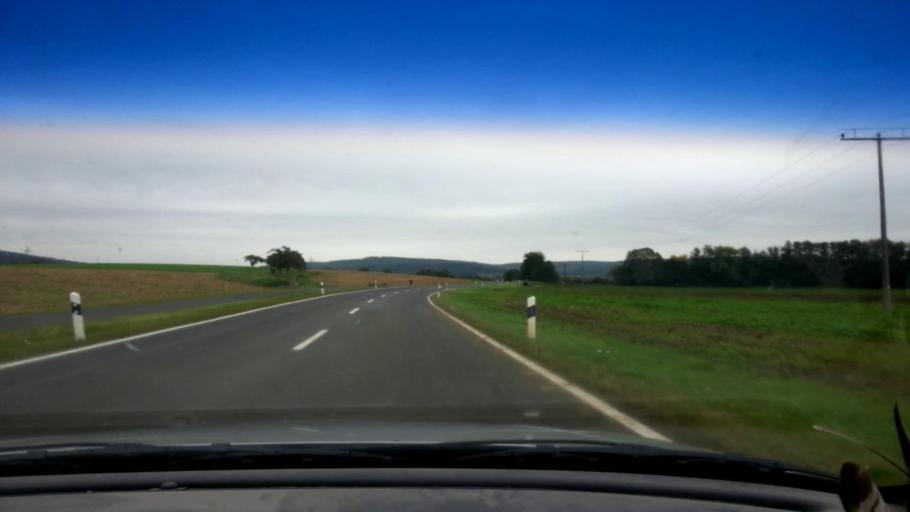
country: DE
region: Bavaria
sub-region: Upper Franconia
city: Memmelsdorf
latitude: 49.9163
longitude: 10.9805
